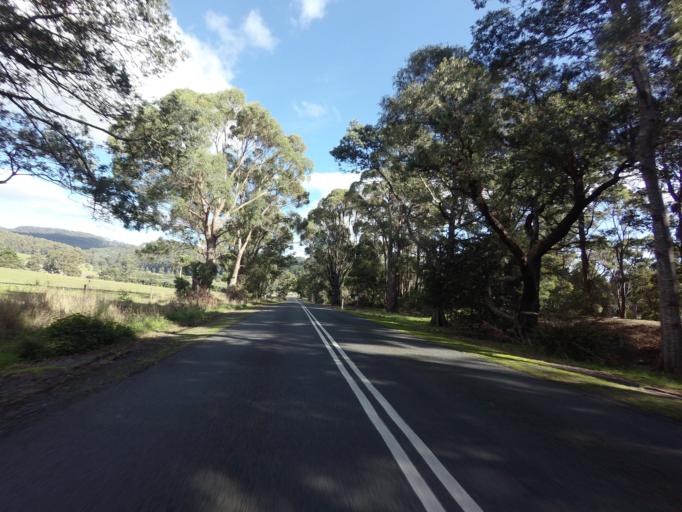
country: AU
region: Tasmania
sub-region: Clarence
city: Sandford
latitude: -43.0623
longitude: 147.8199
